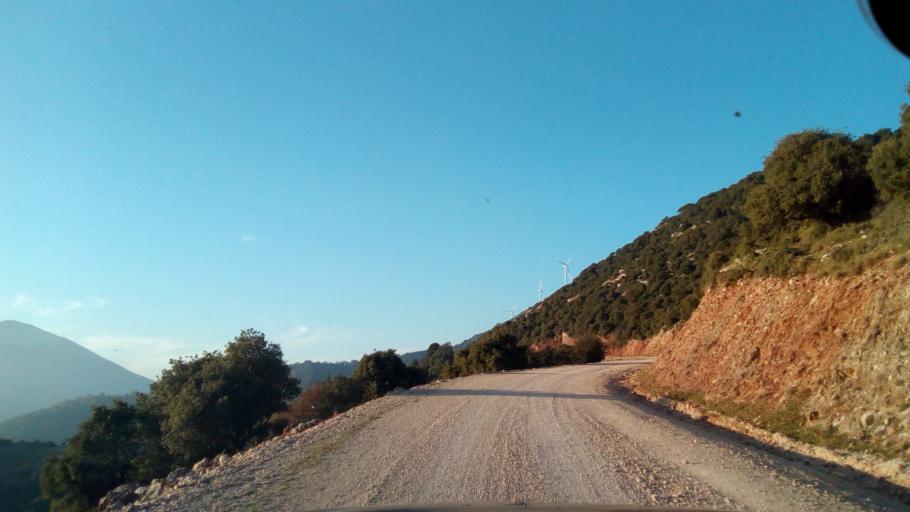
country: GR
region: West Greece
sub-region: Nomos Aitolias kai Akarnanias
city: Nafpaktos
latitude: 38.4398
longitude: 21.8466
